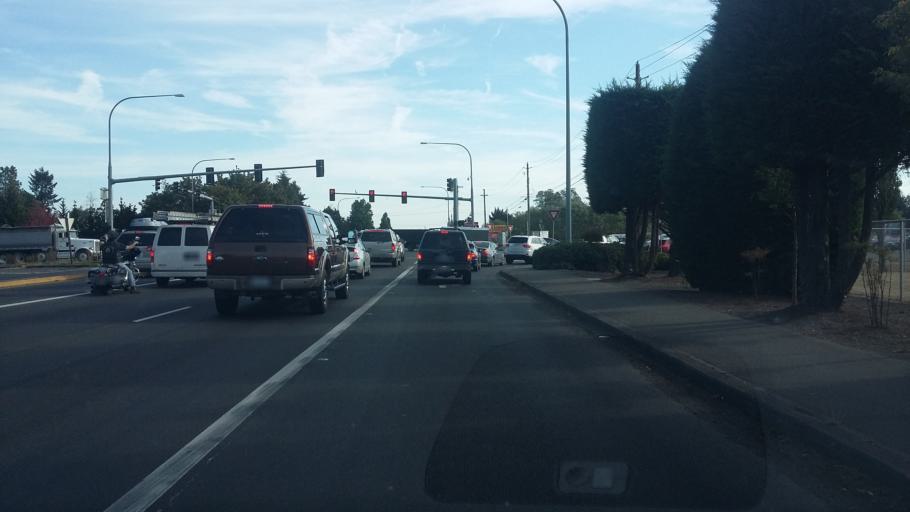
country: US
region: Washington
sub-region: Clark County
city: Orchards
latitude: 45.6828
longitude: -122.5527
